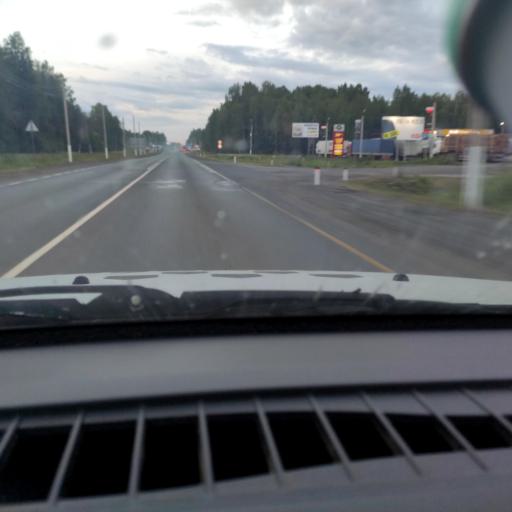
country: RU
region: Kirov
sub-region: Kirovo-Chepetskiy Rayon
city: Kirov
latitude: 58.6832
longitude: 49.6420
